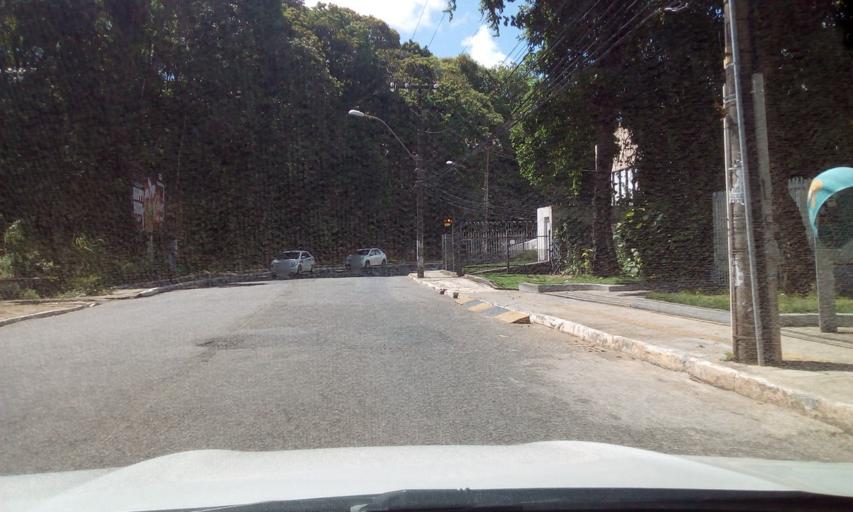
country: BR
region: Bahia
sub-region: Salvador
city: Salvador
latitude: -12.9927
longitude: -38.4661
